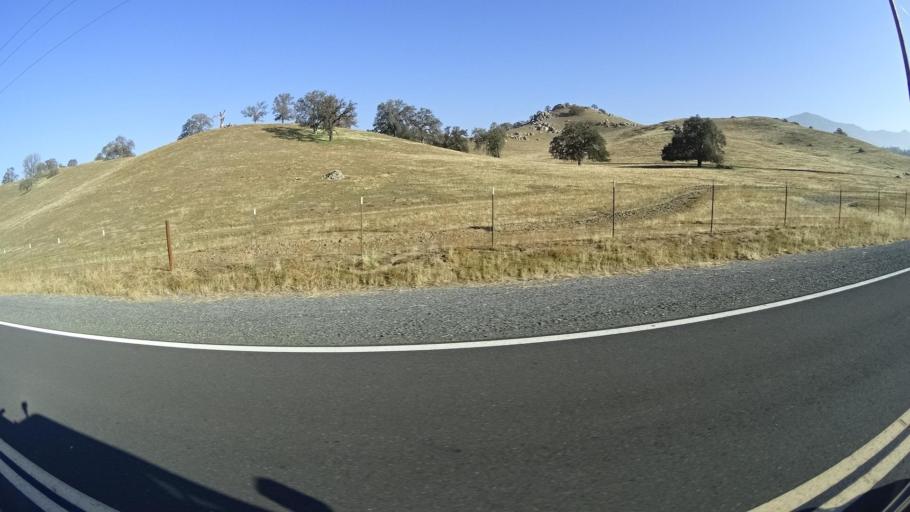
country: US
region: California
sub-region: Tulare County
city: Richgrove
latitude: 35.7386
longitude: -118.8642
